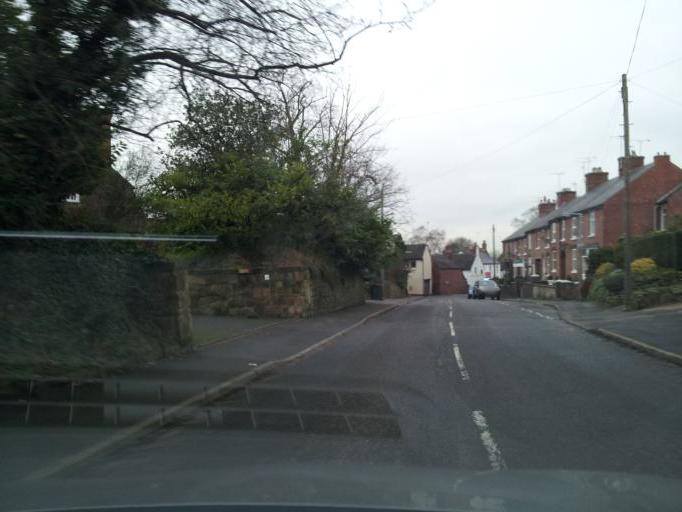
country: GB
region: England
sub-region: Derbyshire
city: Repton
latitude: 52.8398
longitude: -1.5457
